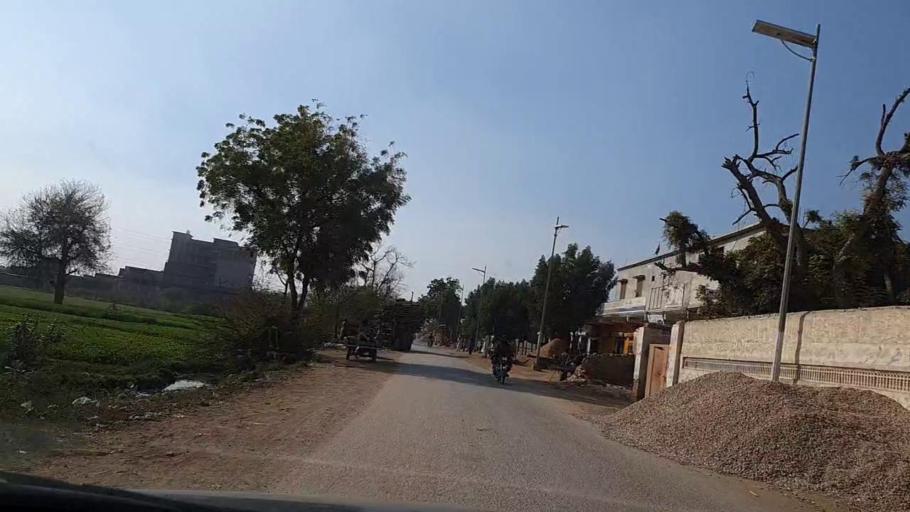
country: PK
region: Sindh
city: Sakrand
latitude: 26.1378
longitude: 68.2647
